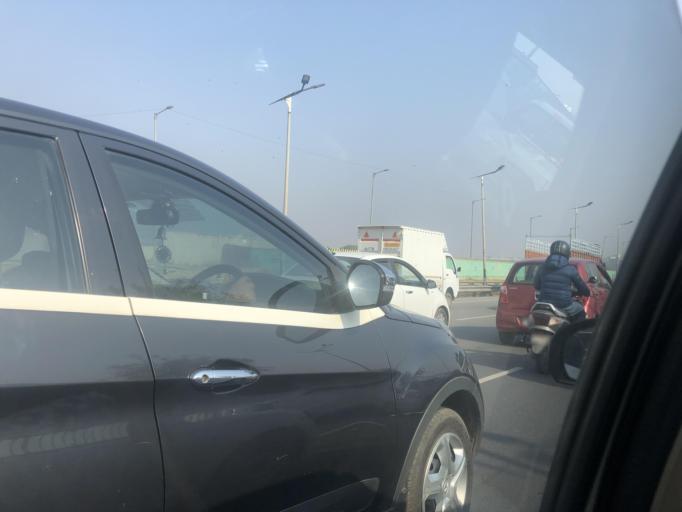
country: IN
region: Haryana
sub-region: Gurgaon
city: Gurgaon
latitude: 28.5363
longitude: 77.1130
